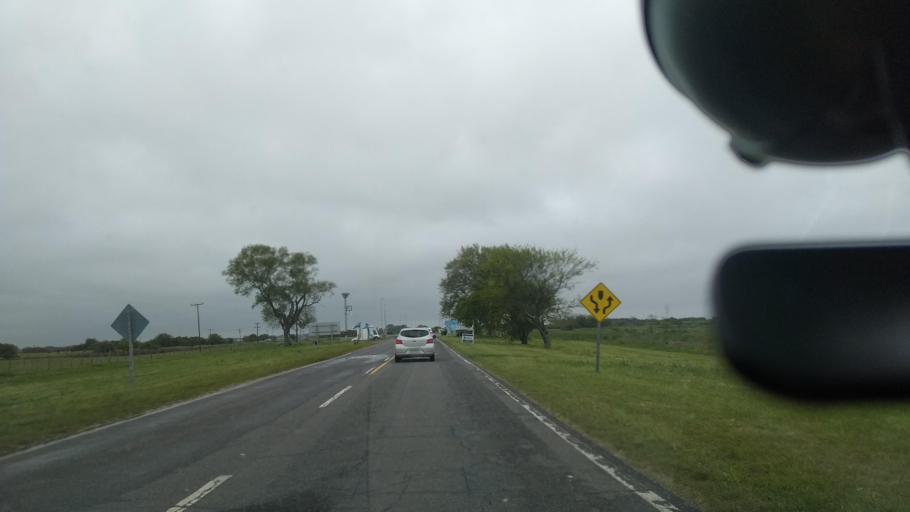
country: AR
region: Buenos Aires
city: Veronica
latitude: -35.5954
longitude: -57.2701
